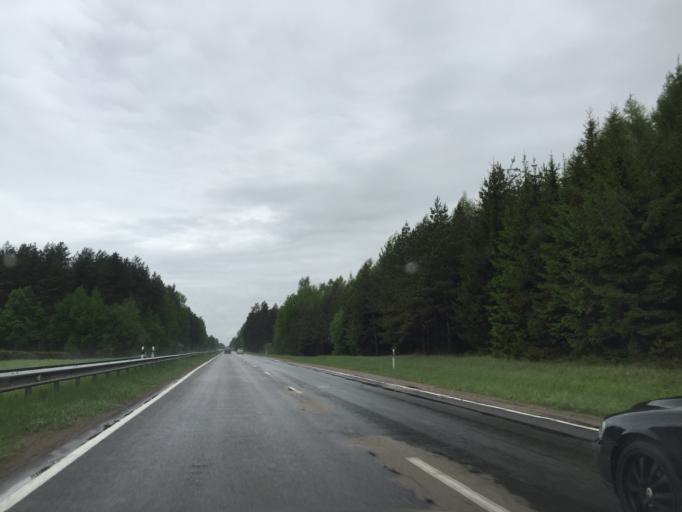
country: LV
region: Ikskile
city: Ikskile
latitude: 56.8288
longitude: 24.5185
